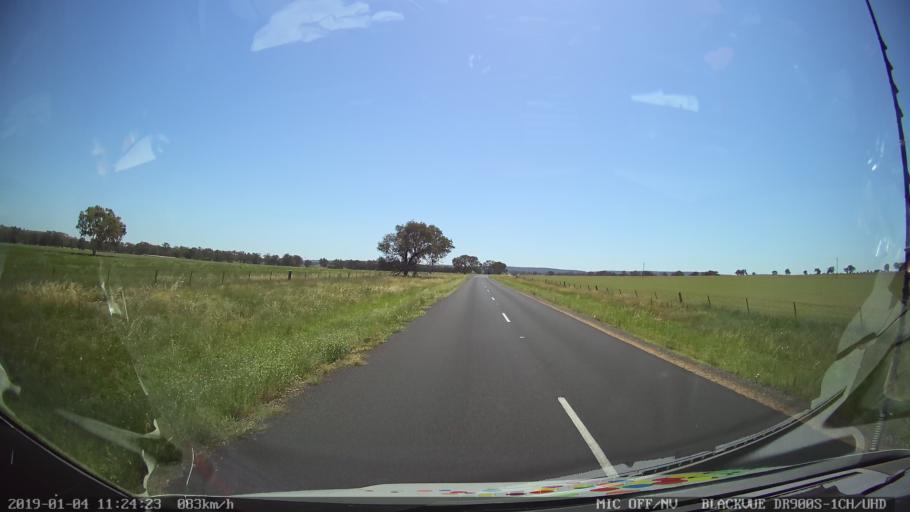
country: AU
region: New South Wales
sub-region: Cabonne
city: Molong
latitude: -33.1329
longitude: 148.7461
